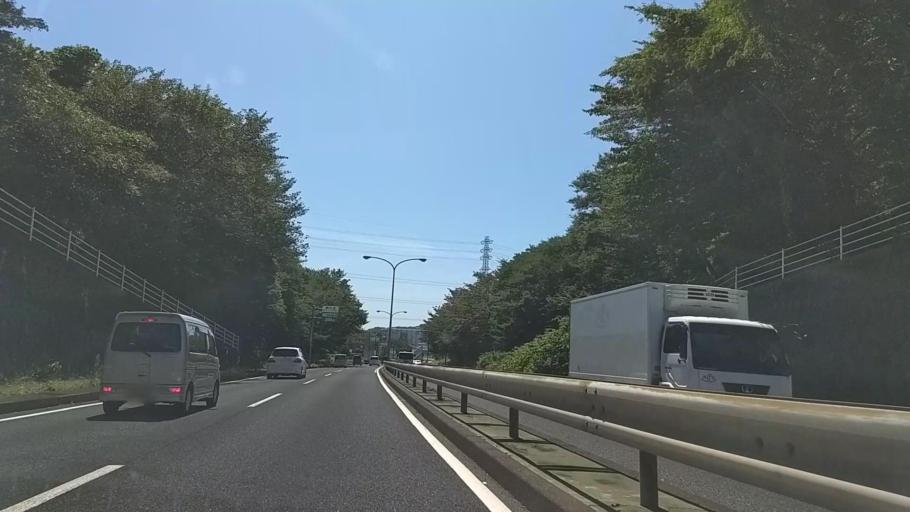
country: JP
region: Kanagawa
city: Zama
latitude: 35.5330
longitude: 139.3623
